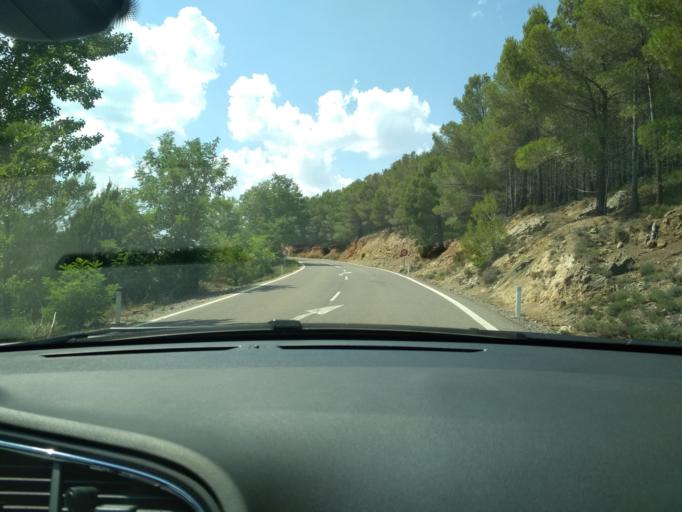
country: ES
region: Aragon
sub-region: Provincia de Teruel
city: Rubielos de Mora
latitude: 40.1856
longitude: -0.6463
